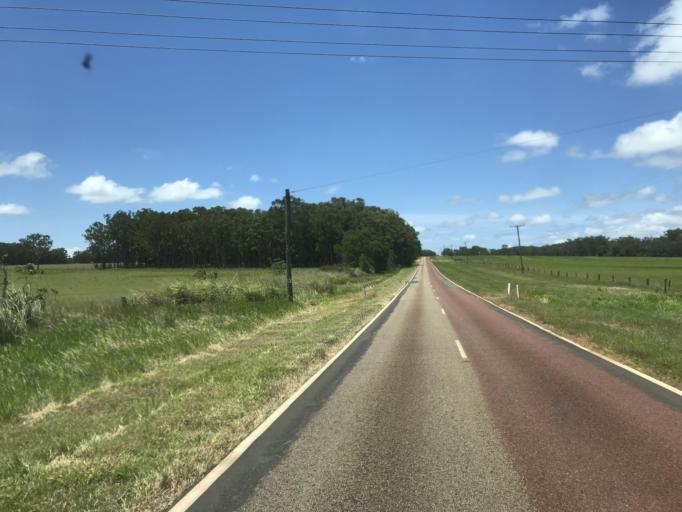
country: AU
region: Queensland
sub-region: Tablelands
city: Ravenshoe
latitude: -17.5263
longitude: 145.4539
